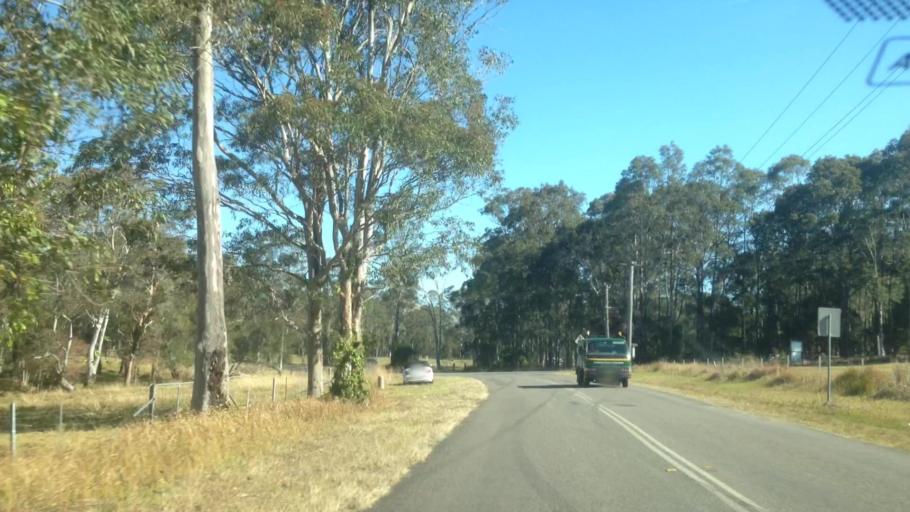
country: AU
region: New South Wales
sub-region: Lake Macquarie Shire
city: Cooranbong
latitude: -33.1156
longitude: 151.4467
